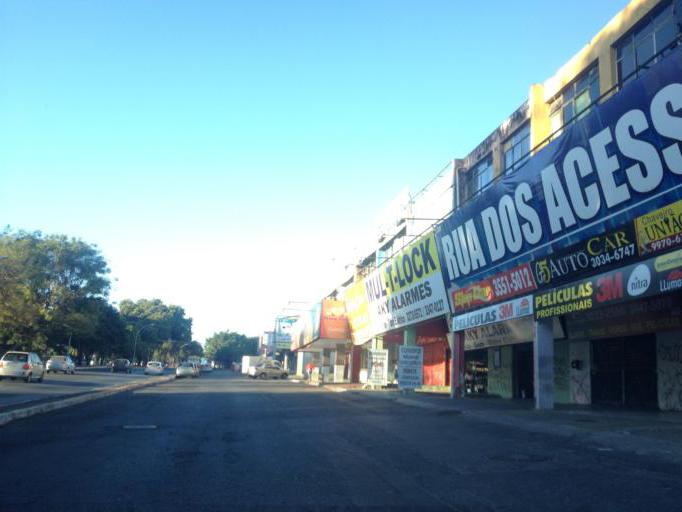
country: BR
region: Federal District
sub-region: Brasilia
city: Brasilia
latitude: -15.7672
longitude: -47.8901
